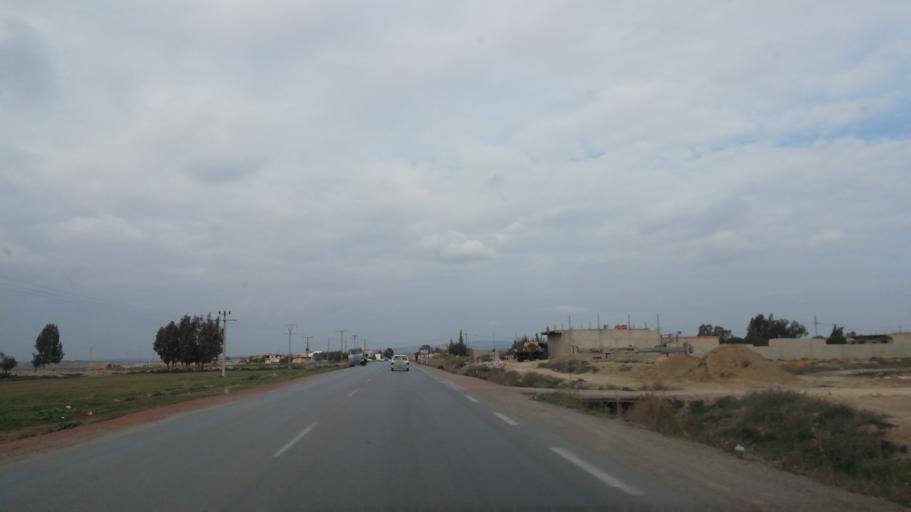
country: DZ
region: Mostaganem
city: Mostaganem
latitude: 35.6923
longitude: 0.0559
